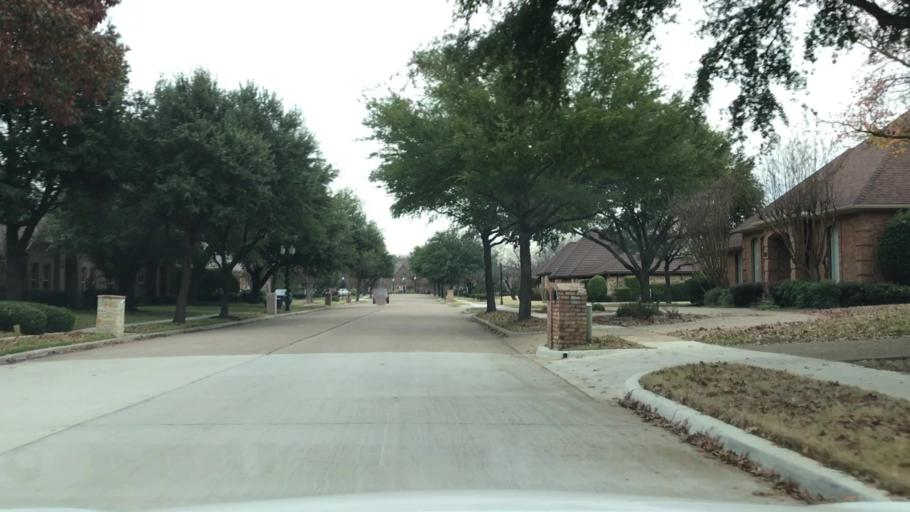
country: US
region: Texas
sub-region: Dallas County
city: Coppell
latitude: 32.9114
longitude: -96.9791
